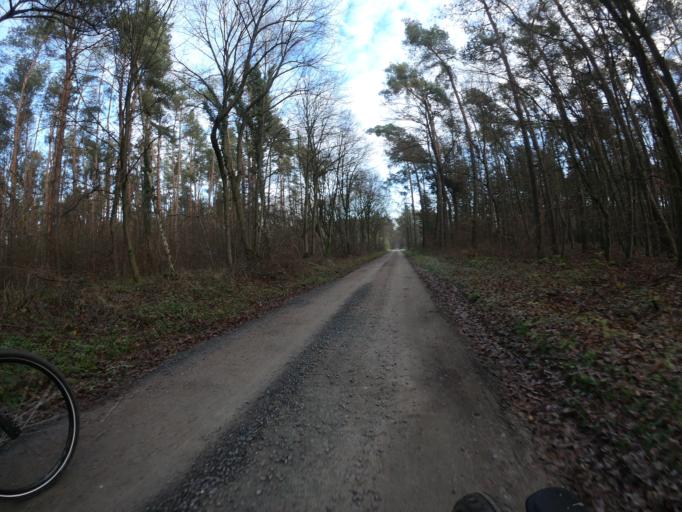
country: DE
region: Hesse
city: Morfelden-Walldorf
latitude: 49.9629
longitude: 8.5869
